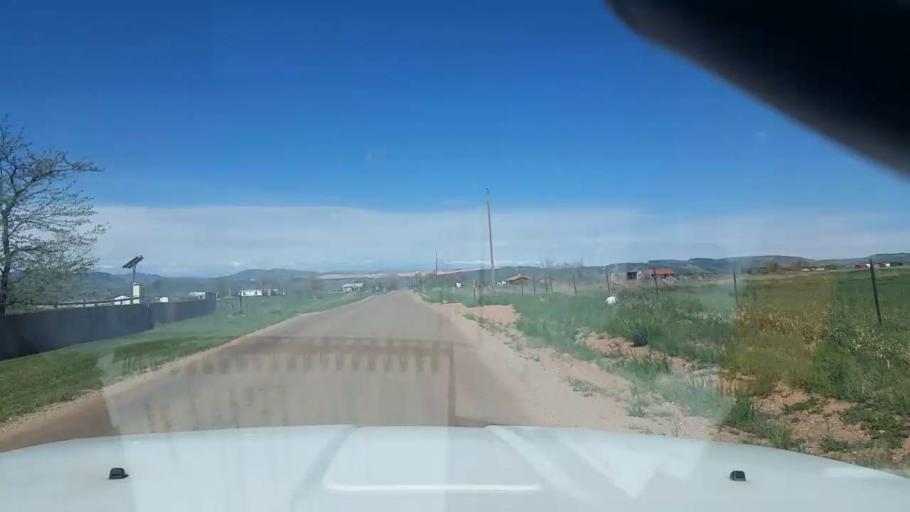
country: US
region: Colorado
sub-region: Larimer County
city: Wellington
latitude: 40.7839
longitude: -105.0826
